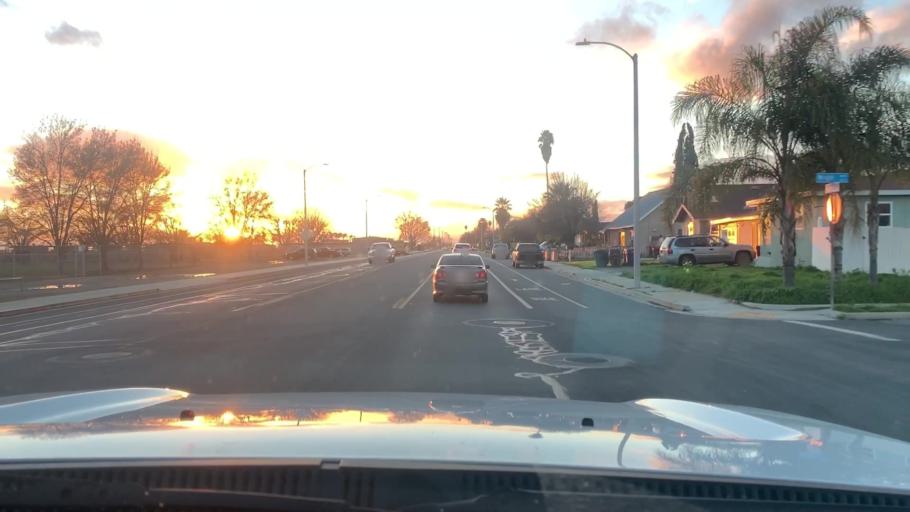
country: US
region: California
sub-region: Tulare County
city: Tulare
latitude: 36.1965
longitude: -119.3534
